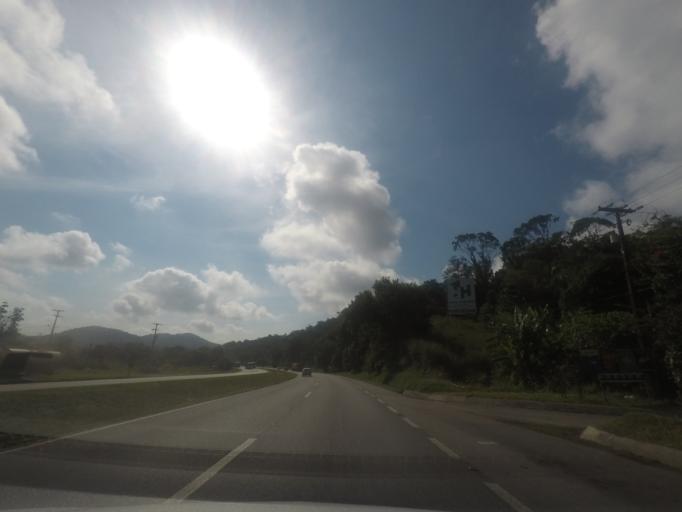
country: BR
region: Parana
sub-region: Antonina
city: Antonina
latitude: -25.5448
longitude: -48.7804
